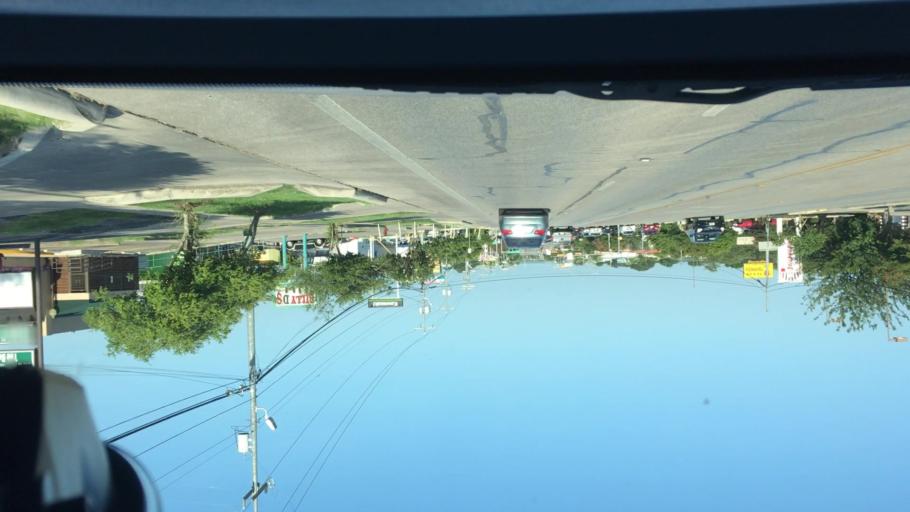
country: US
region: Texas
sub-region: Bexar County
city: Universal City
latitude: 29.5533
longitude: -98.3086
